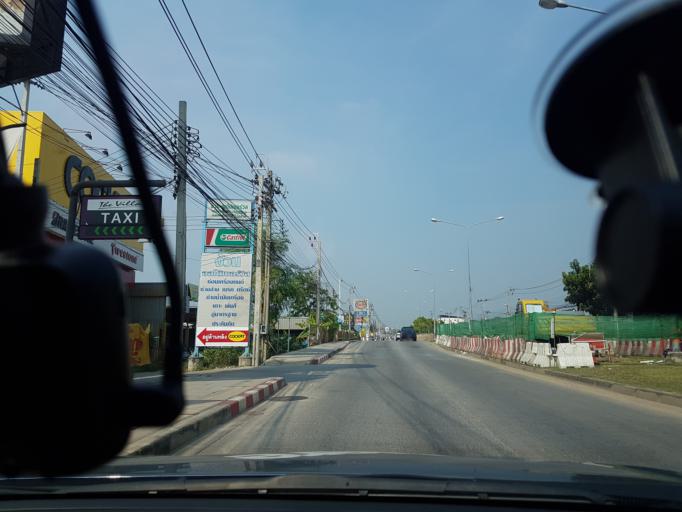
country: TH
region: Bangkok
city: Khlong Sam Wa
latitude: 13.8461
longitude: 100.7208
